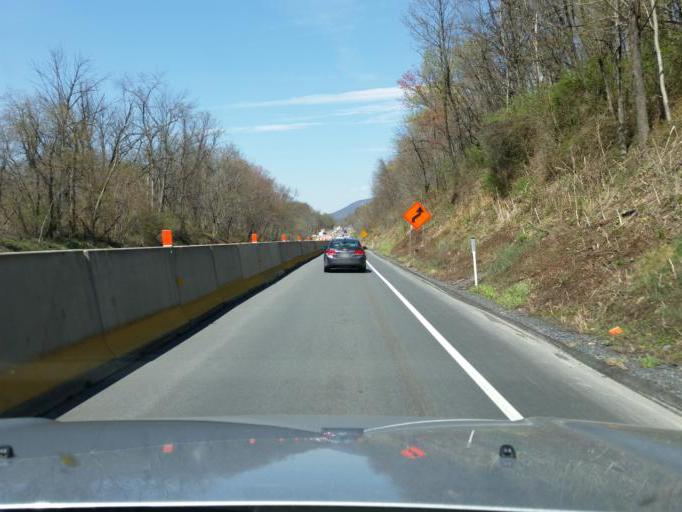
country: US
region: Pennsylvania
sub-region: Mifflin County
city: Lewistown
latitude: 40.5820
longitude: -77.5542
